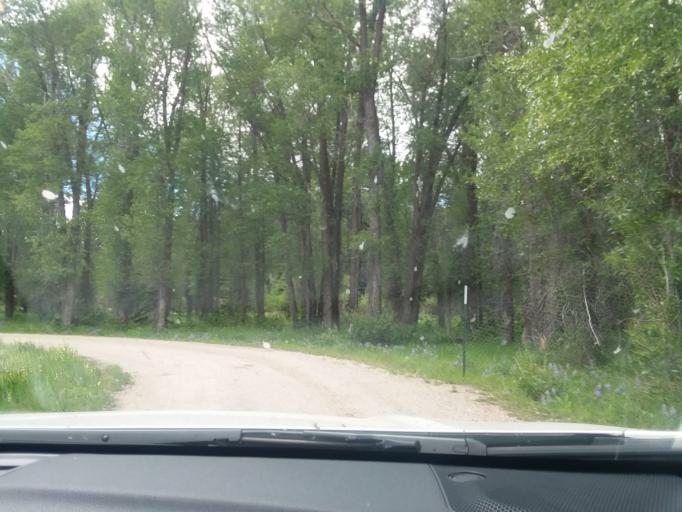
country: US
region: Wyoming
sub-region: Teton County
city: Moose Wilson Road
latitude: 43.5051
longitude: -110.8432
